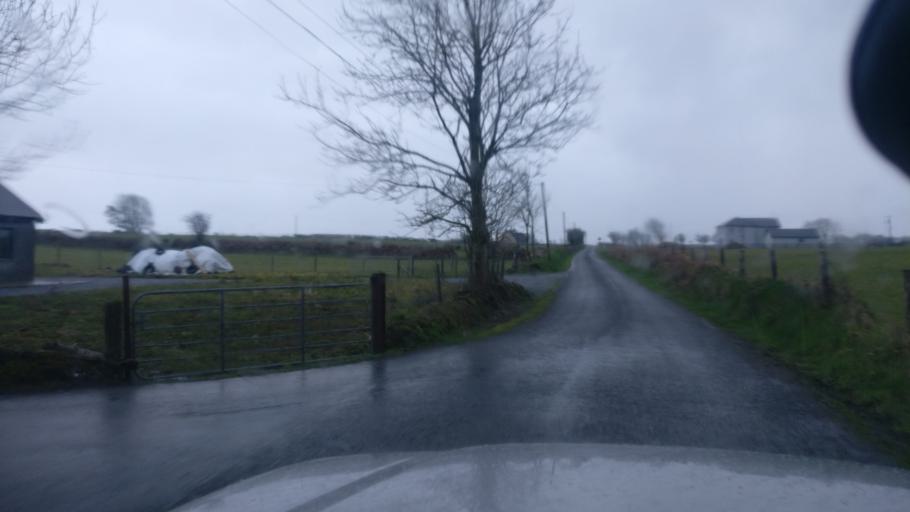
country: IE
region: Connaught
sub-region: County Galway
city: Loughrea
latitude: 53.2328
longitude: -8.4238
